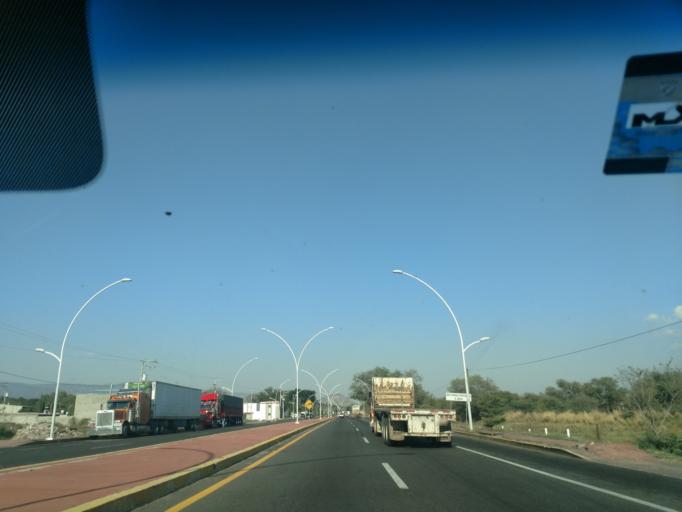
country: MX
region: Nayarit
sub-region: Ahuacatlan
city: Ahuacatlan
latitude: 21.0587
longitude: -104.4941
